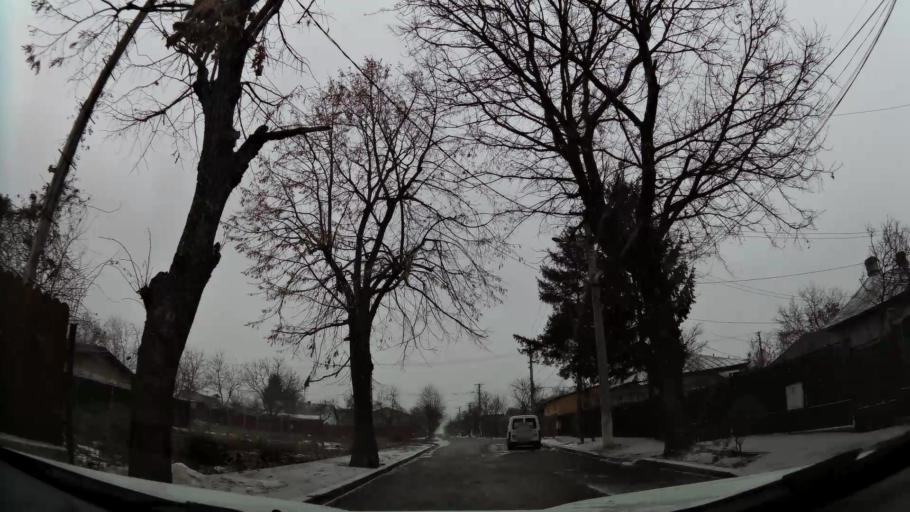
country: RO
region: Prahova
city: Ploiesti
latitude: 44.9529
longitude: 26.0374
